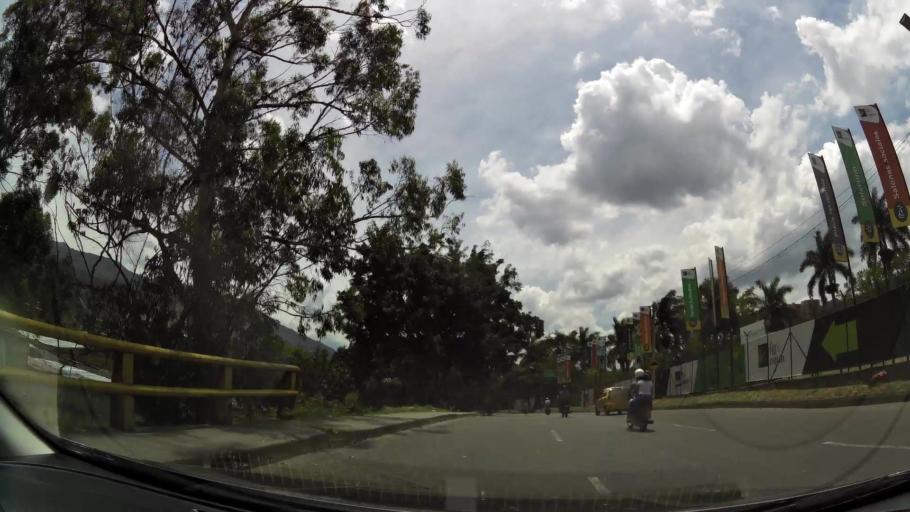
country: CO
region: Antioquia
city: Bello
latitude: 6.3312
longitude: -75.5597
